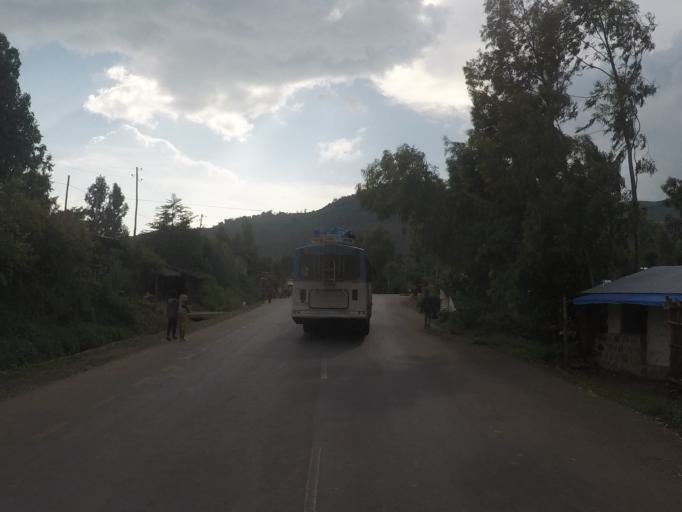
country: ET
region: Amhara
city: Gondar
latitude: 12.6441
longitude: 37.4810
